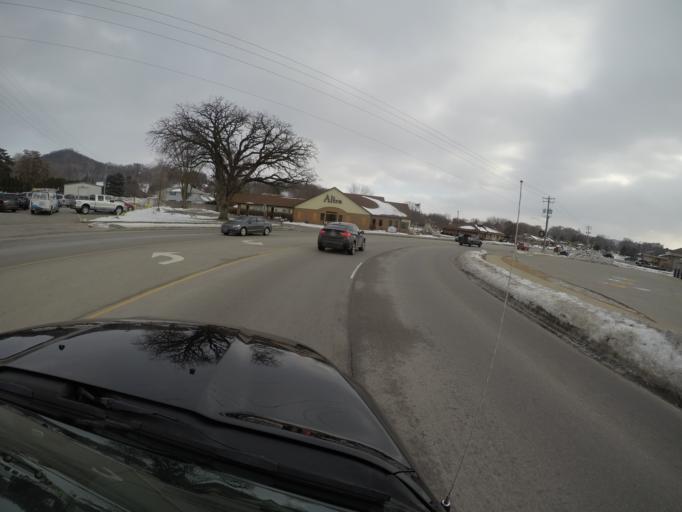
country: US
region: Wisconsin
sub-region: La Crosse County
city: Onalaska
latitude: 43.8837
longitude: -91.2092
